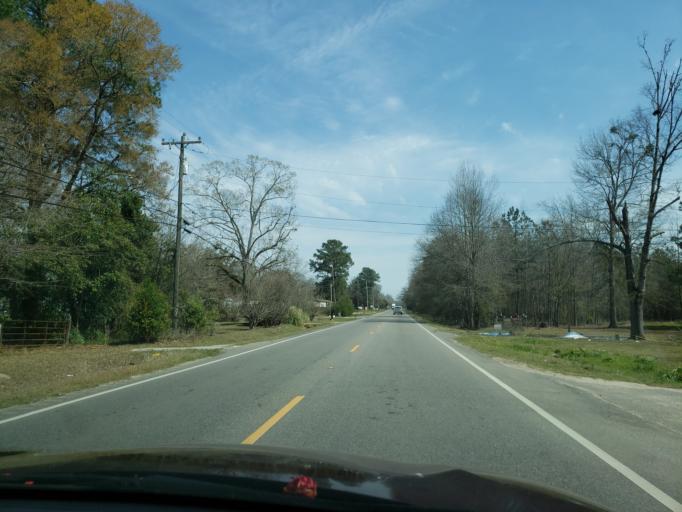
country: US
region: Alabama
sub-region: Autauga County
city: Prattville
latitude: 32.4320
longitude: -86.4877
